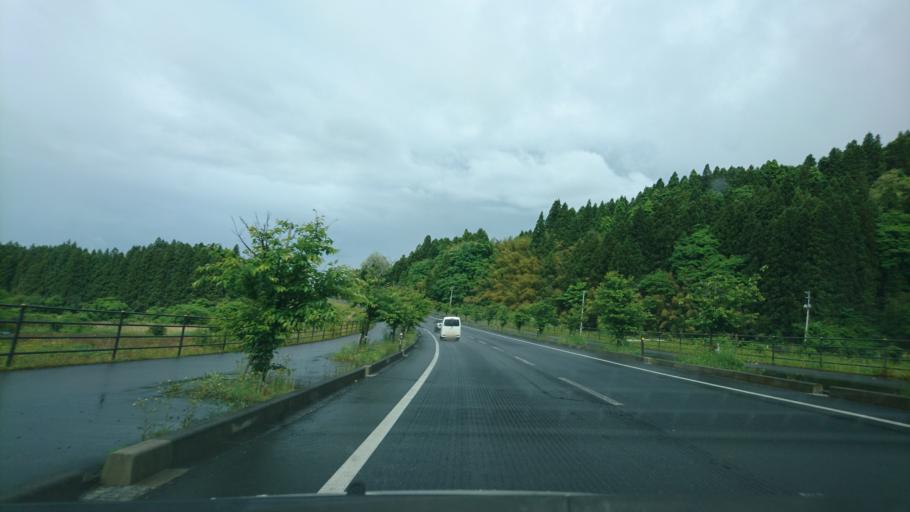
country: JP
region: Iwate
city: Ichinoseki
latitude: 38.9414
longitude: 141.0787
